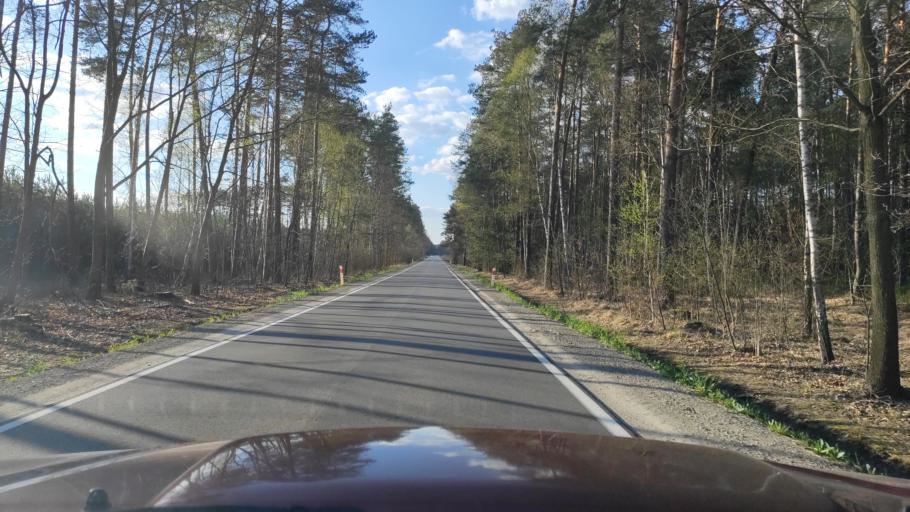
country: PL
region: Masovian Voivodeship
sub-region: Powiat zwolenski
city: Zwolen
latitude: 51.3928
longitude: 21.5467
